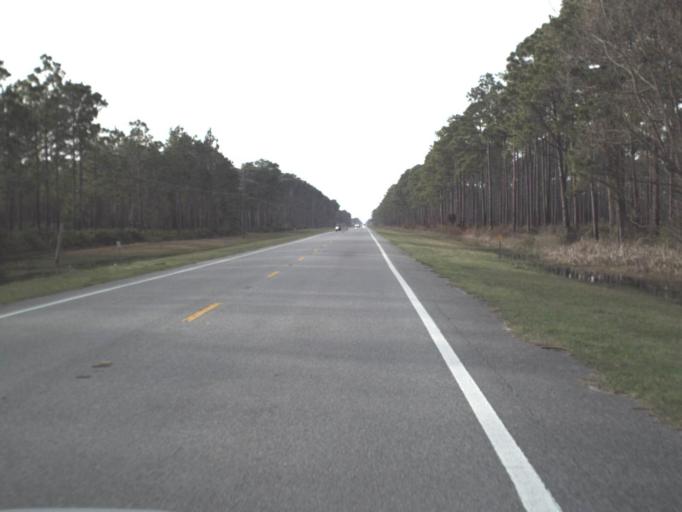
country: US
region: Florida
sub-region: Bay County
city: Mexico Beach
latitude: 30.0065
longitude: -85.5079
